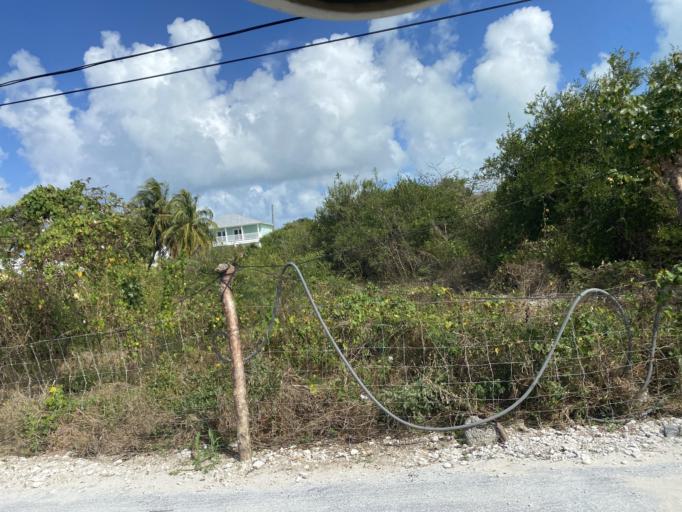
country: BS
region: Spanish Wells
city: Spanish Wells
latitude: 25.5462
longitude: -76.7757
